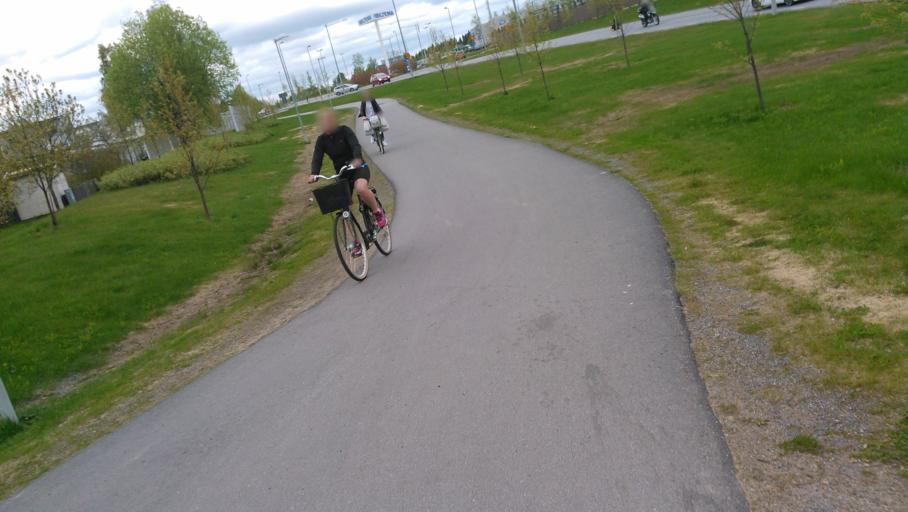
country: SE
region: Vaesterbotten
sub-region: Umea Kommun
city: Ersmark
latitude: 63.8460
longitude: 20.3134
